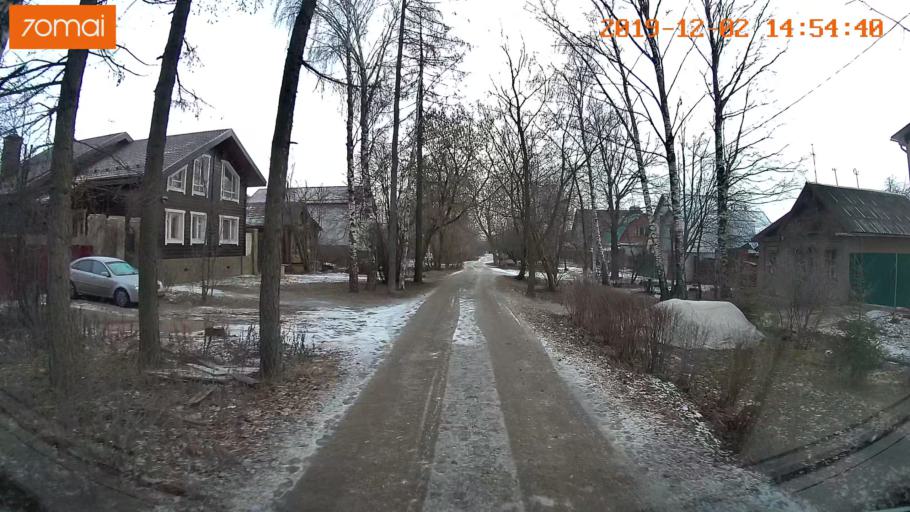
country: RU
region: Ivanovo
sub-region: Gorod Ivanovo
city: Ivanovo
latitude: 56.9750
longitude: 41.0157
